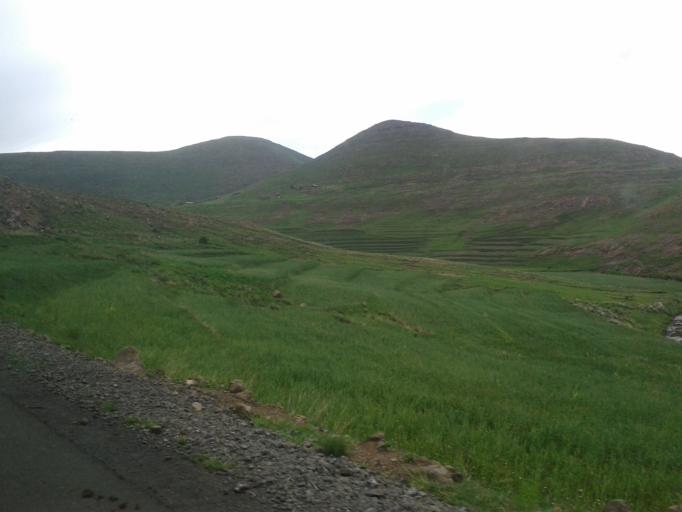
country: LS
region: Maseru
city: Nako
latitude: -29.8038
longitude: 28.0300
